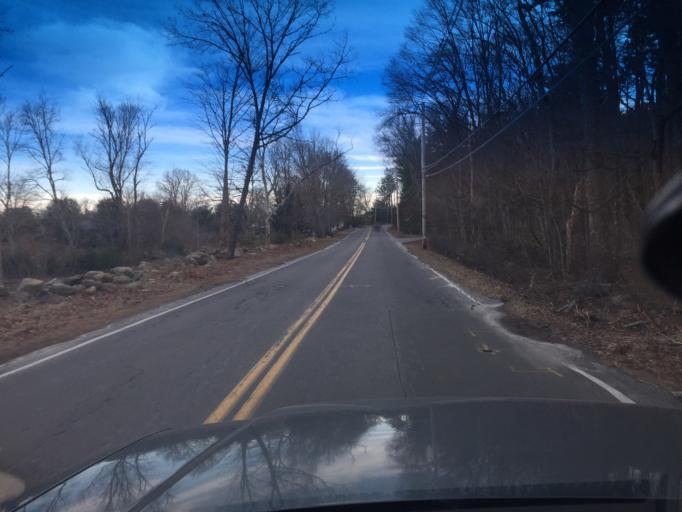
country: US
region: Massachusetts
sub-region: Middlesex County
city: Holliston
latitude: 42.1939
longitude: -71.4175
